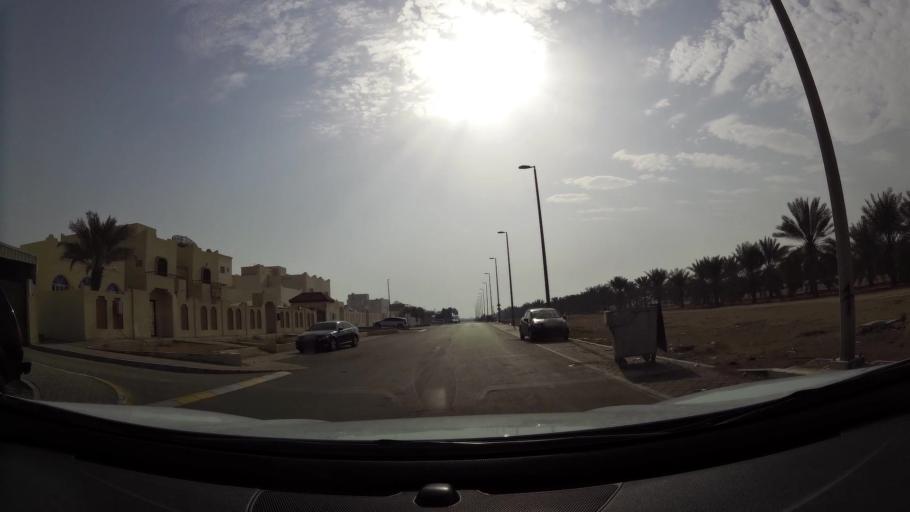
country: AE
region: Abu Dhabi
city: Abu Dhabi
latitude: 24.2381
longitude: 54.7220
